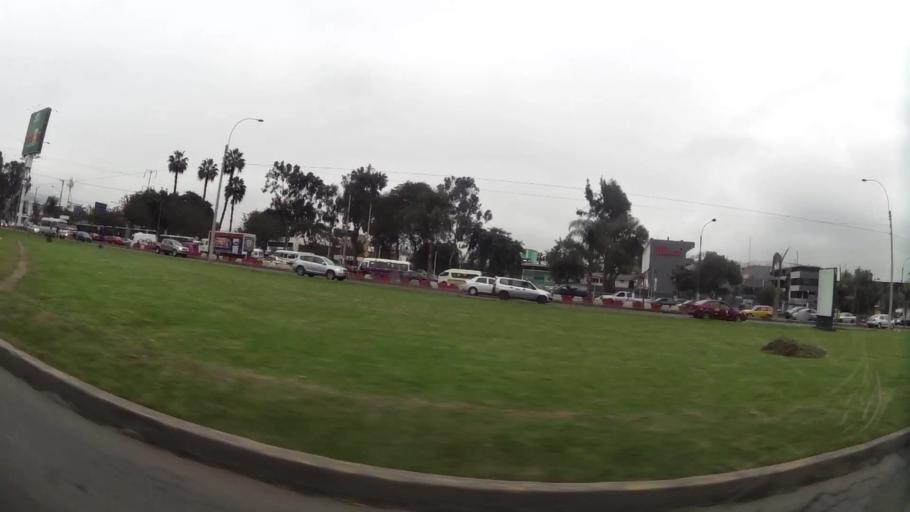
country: PE
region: Lima
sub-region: Lima
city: La Molina
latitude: -12.0718
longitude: -76.9581
